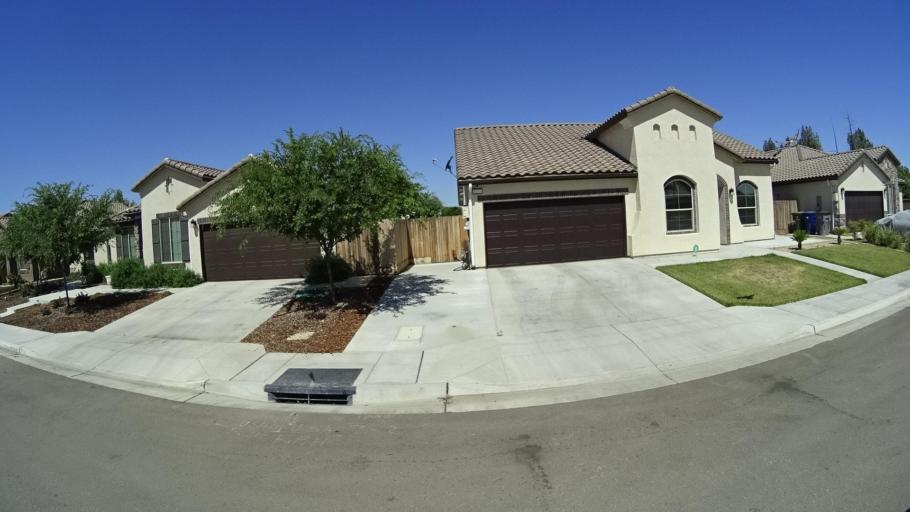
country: US
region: California
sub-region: Fresno County
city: Sunnyside
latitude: 36.7177
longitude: -119.6724
